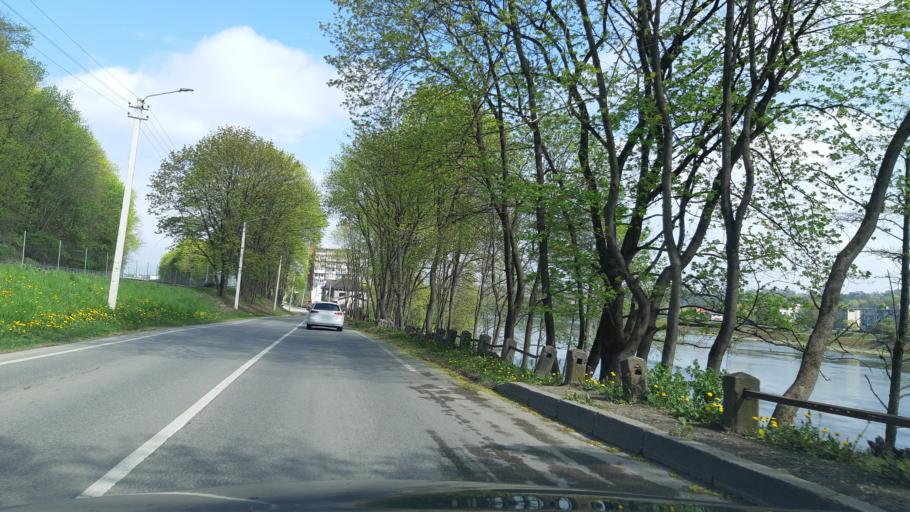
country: LT
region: Kauno apskritis
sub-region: Kaunas
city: Aleksotas
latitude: 54.8709
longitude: 23.9251
